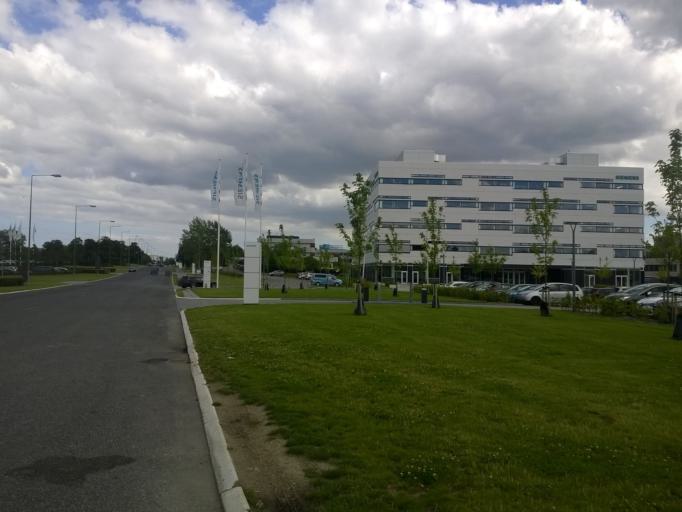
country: DK
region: Capital Region
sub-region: Ballerup Kommune
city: Ballerup
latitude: 55.7331
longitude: 12.3787
